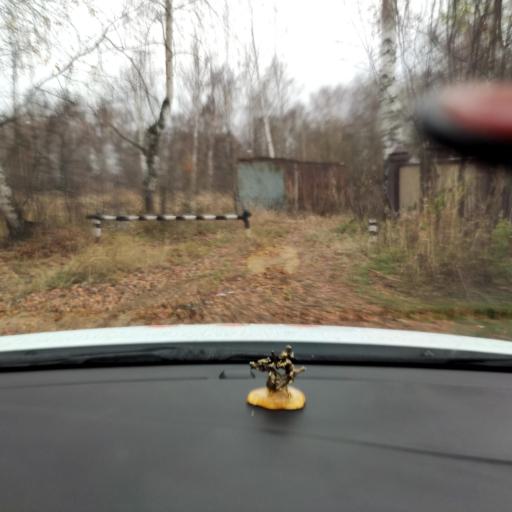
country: RU
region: Tatarstan
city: Vysokaya Gora
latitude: 55.8468
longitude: 49.2387
